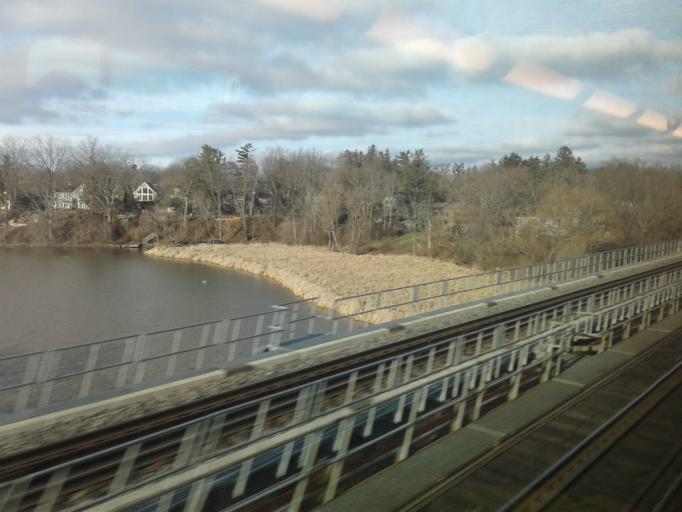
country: CA
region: Ontario
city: Mississauga
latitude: 43.5516
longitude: -79.5921
